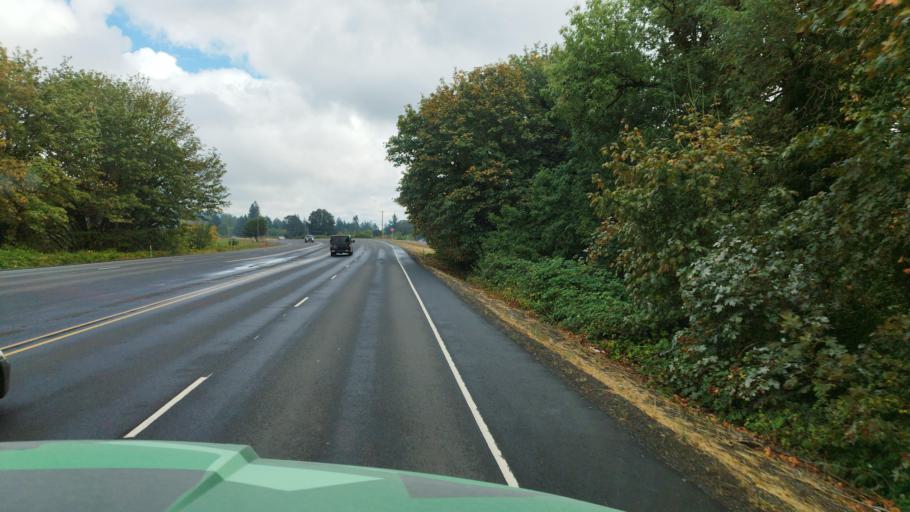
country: US
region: Oregon
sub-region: Yamhill County
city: Lafayette
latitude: 45.2399
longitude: -123.1440
